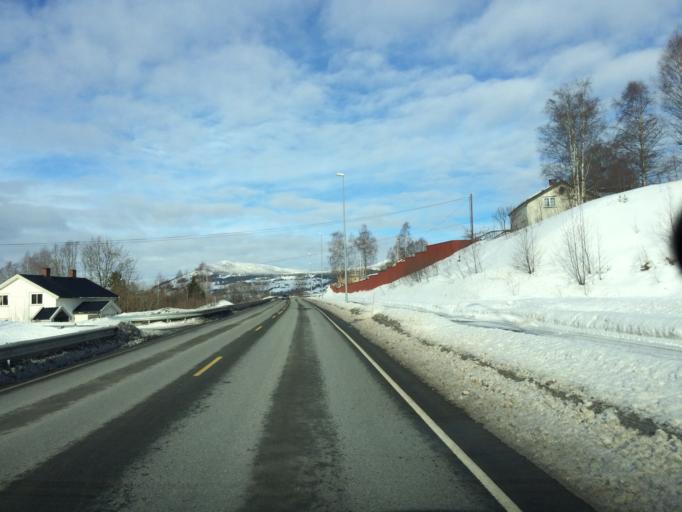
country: NO
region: Oppland
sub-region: Gausdal
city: Segalstad bru
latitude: 61.1949
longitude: 10.3119
